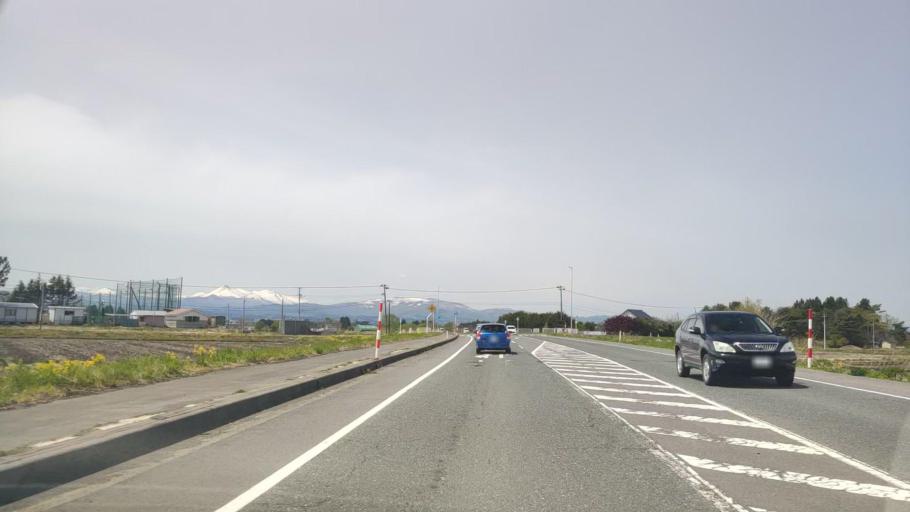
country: JP
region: Aomori
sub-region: Misawa Shi
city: Inuotose
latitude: 40.6380
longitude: 141.2395
